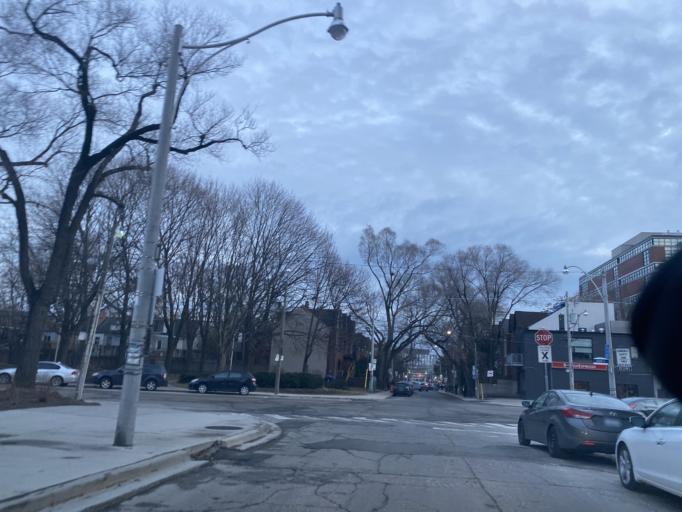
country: CA
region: Ontario
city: Toronto
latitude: 43.6587
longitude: -79.3596
